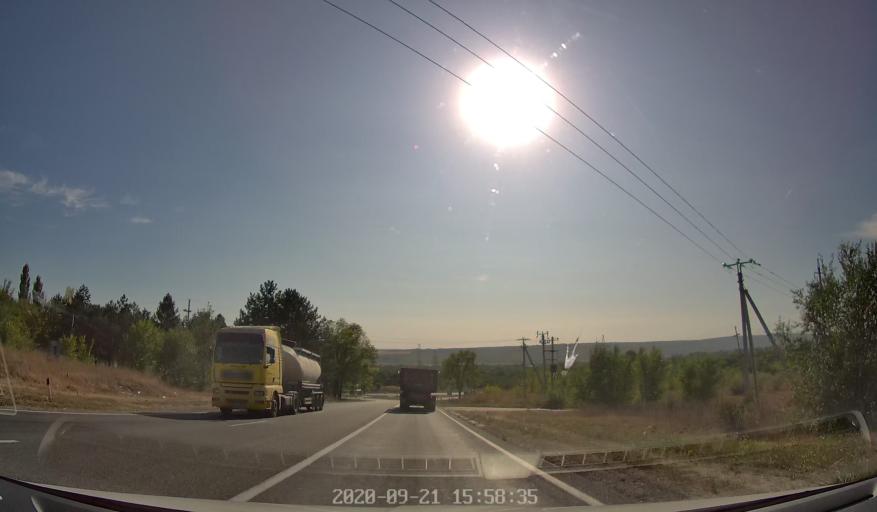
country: MD
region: Orhei
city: Orhei
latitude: 47.3950
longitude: 28.7999
